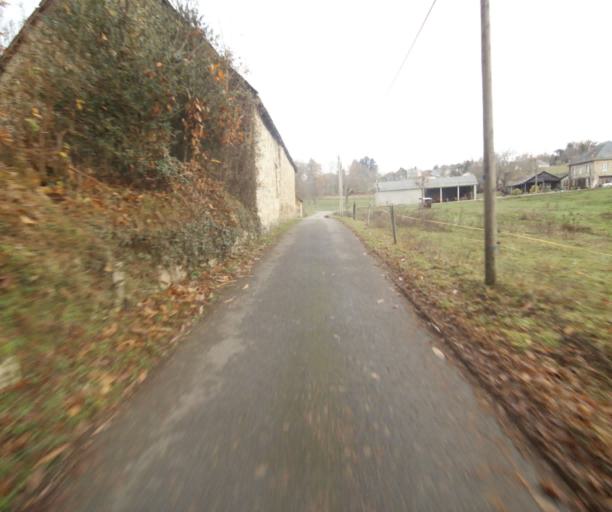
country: FR
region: Limousin
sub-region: Departement de la Correze
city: Chameyrat
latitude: 45.2330
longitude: 1.6956
